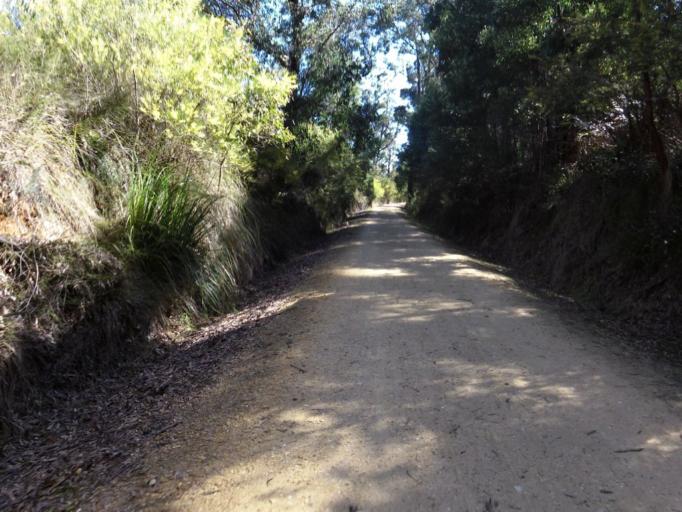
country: AU
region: Victoria
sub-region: Latrobe
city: Moe
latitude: -38.3749
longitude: 146.2286
